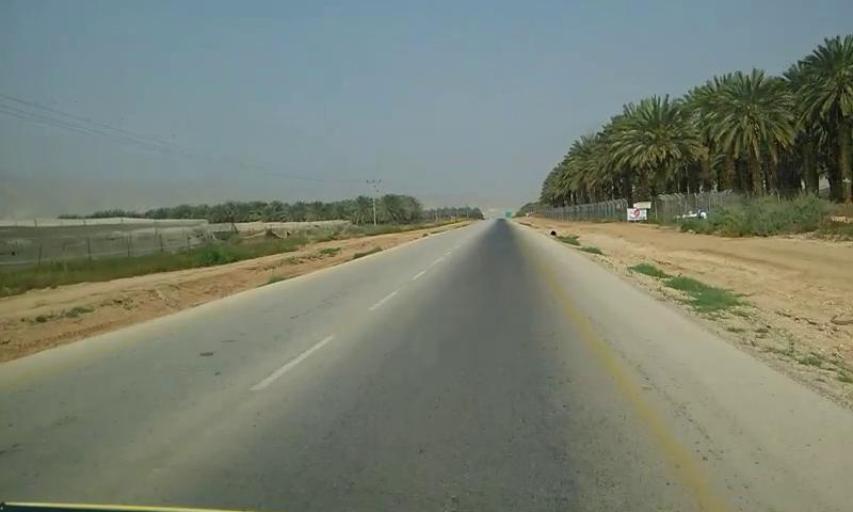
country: PS
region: West Bank
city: Al Fasayil
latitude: 31.9937
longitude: 35.4577
